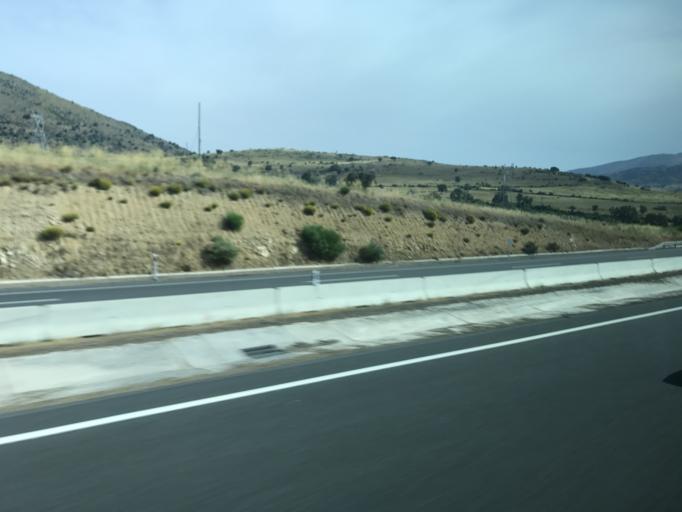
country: ES
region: Castille and Leon
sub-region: Provincia de Segovia
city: Vegas de Matute
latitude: 40.7375
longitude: -4.2645
